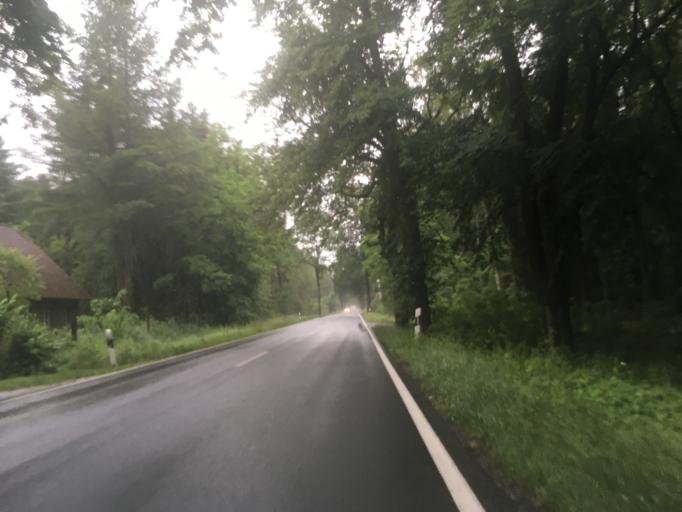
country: DE
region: Brandenburg
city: Marienwerder
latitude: 52.9353
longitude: 13.5524
